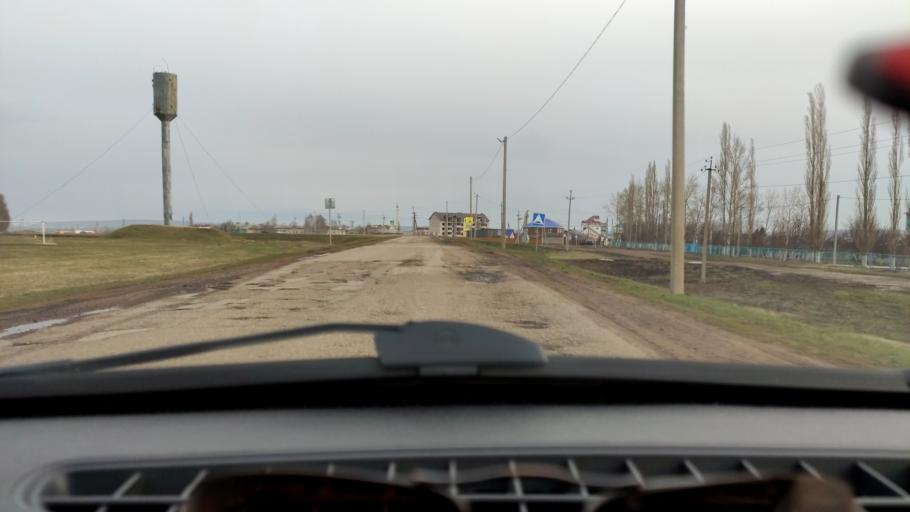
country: RU
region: Bashkortostan
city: Kabakovo
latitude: 54.5265
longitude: 56.1576
